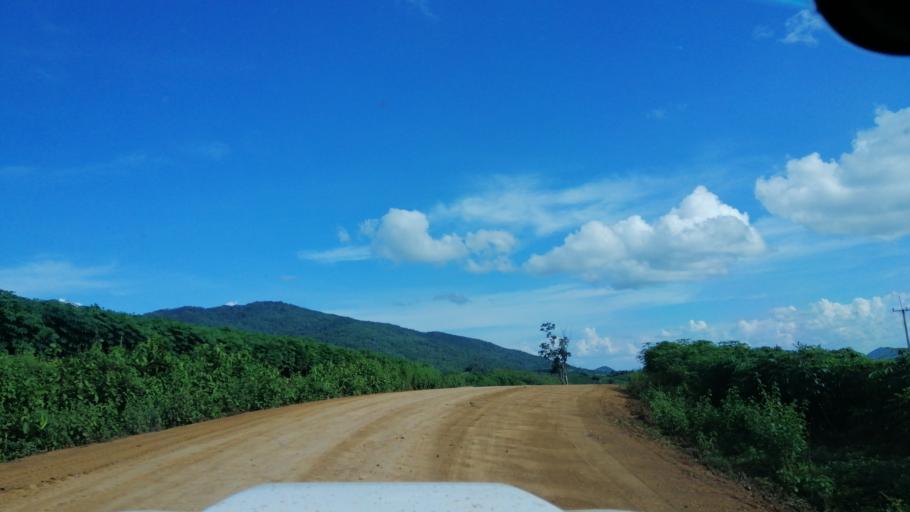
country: TH
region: Uttaradit
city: Ban Khok
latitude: 17.8987
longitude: 101.2151
